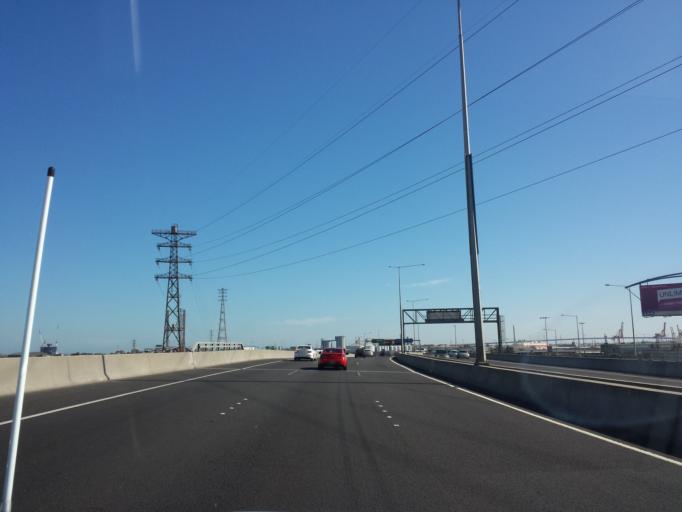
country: AU
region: Victoria
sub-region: Melbourne
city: North Melbourne
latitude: -37.8024
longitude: 144.9360
